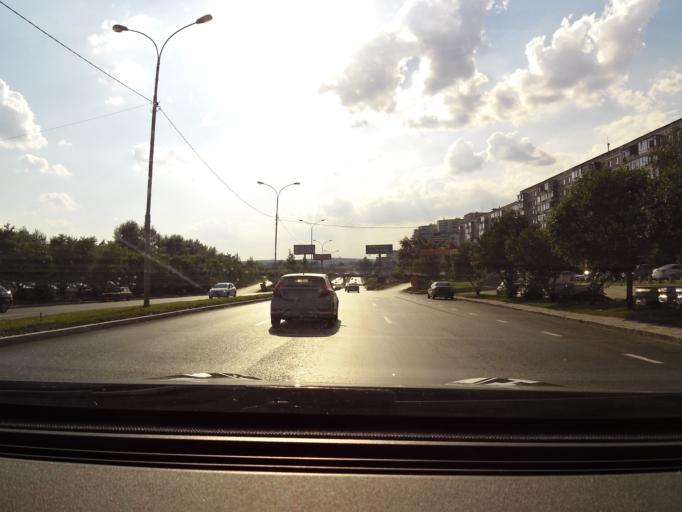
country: RU
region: Sverdlovsk
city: Sovkhoznyy
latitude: 56.8259
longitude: 60.5491
